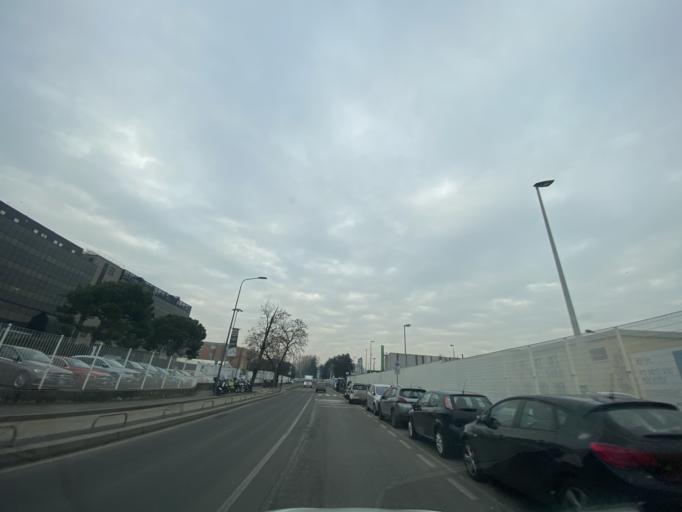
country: IT
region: Lombardy
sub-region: Citta metropolitana di Milano
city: Vimodrone
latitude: 45.5065
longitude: 9.2680
